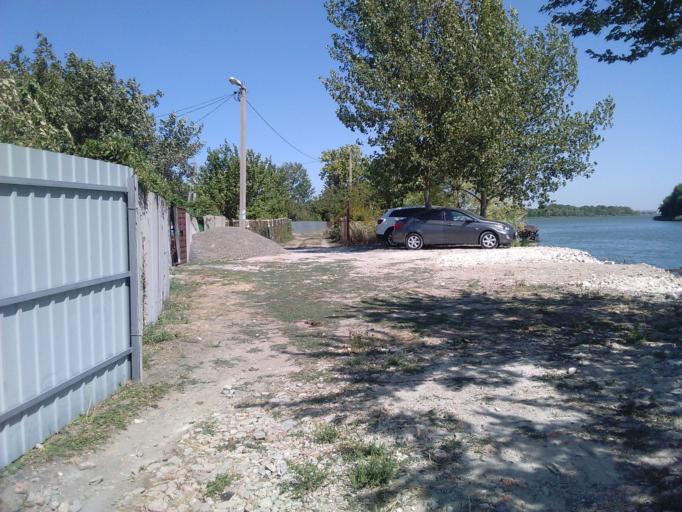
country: RU
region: Rostov
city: Azov
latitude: 47.1326
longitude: 39.4807
